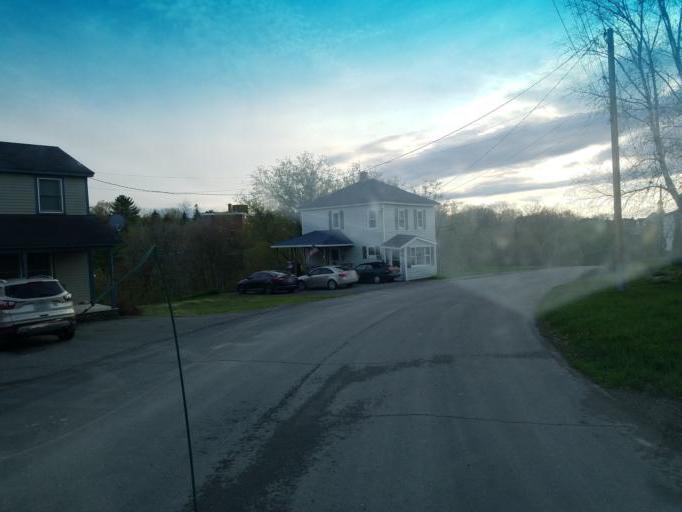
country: US
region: Maine
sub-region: Aroostook County
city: Caribou
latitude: 46.8585
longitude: -68.0066
